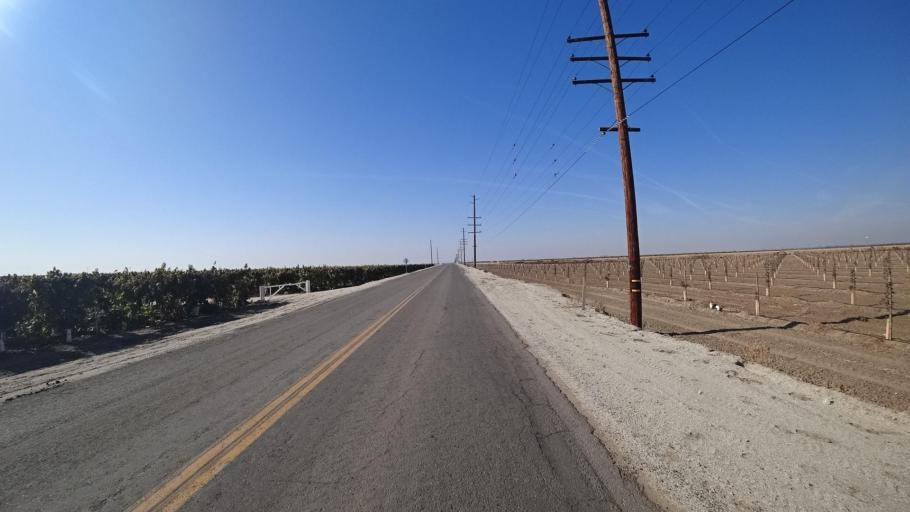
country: US
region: California
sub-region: Kern County
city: McFarland
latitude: 35.7036
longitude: -119.1893
